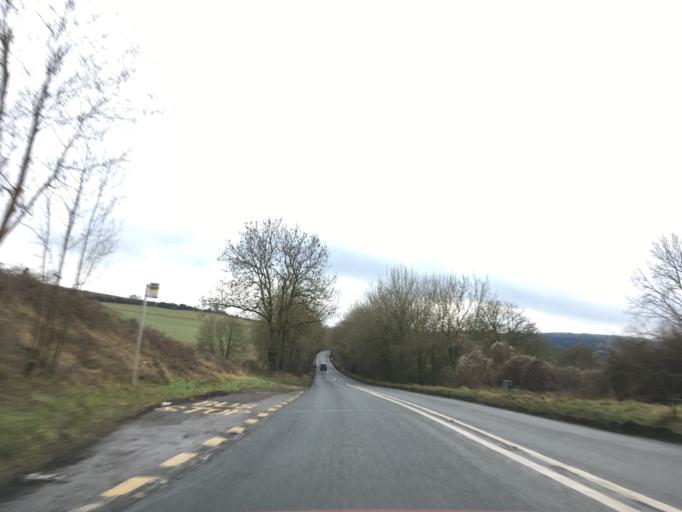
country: GB
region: England
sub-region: Gloucestershire
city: Charlton Kings
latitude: 51.8431
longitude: -2.0472
